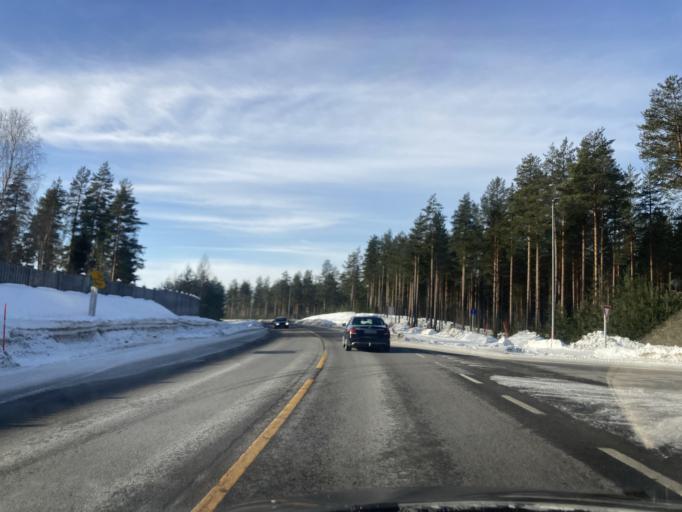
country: NO
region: Hedmark
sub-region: Elverum
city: Elverum
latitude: 60.9058
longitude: 11.6059
